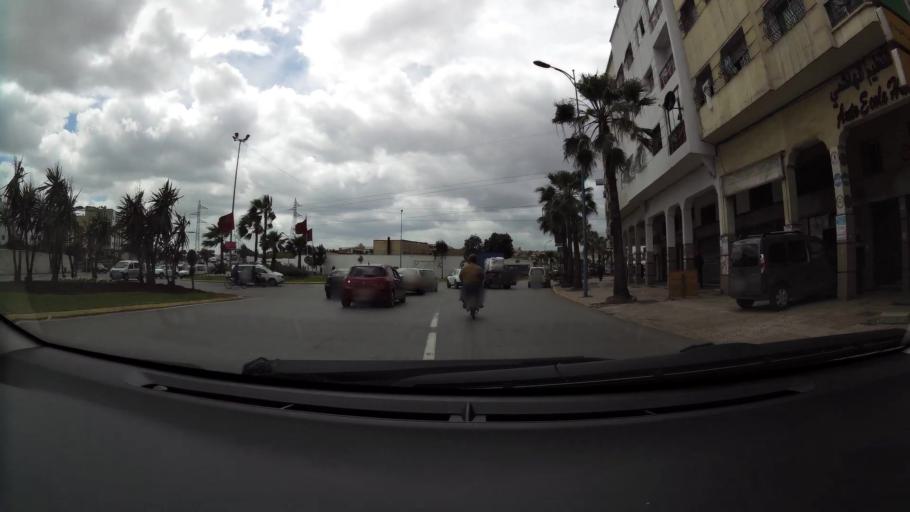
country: MA
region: Grand Casablanca
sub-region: Casablanca
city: Casablanca
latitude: 33.5874
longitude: -7.5456
